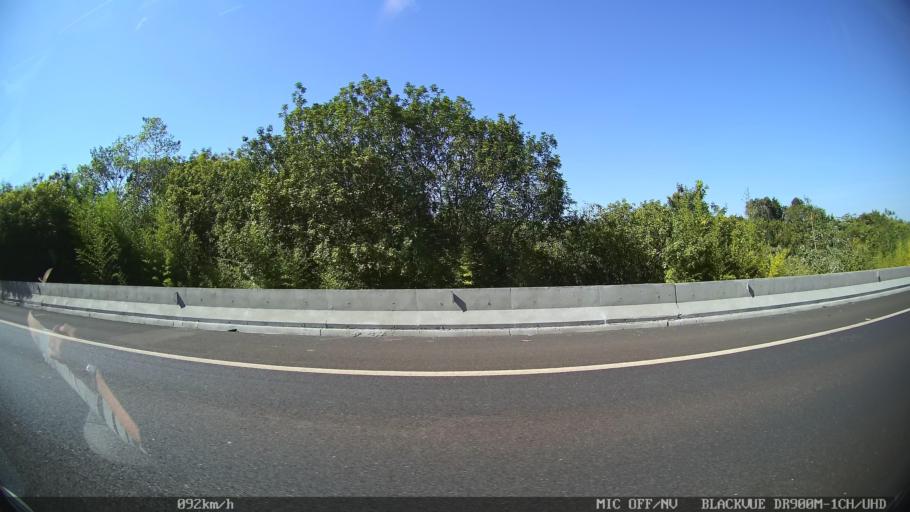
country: BR
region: Sao Paulo
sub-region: Franca
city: Franca
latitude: -20.7043
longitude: -47.5022
